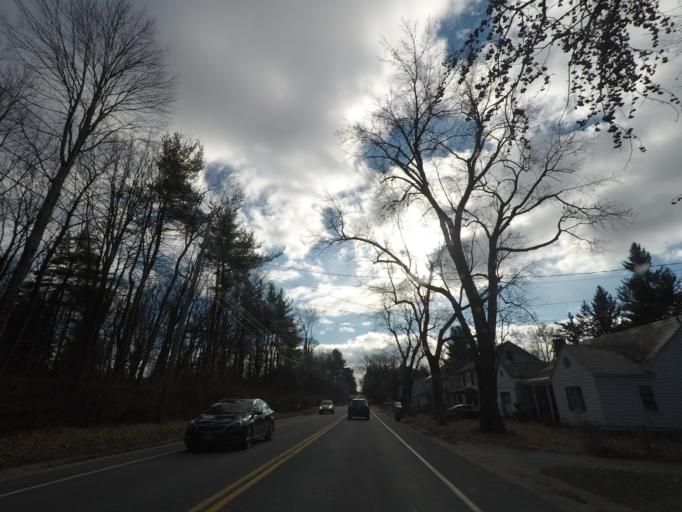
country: US
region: New York
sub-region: Schenectady County
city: Schenectady
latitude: 42.8033
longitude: -73.8931
